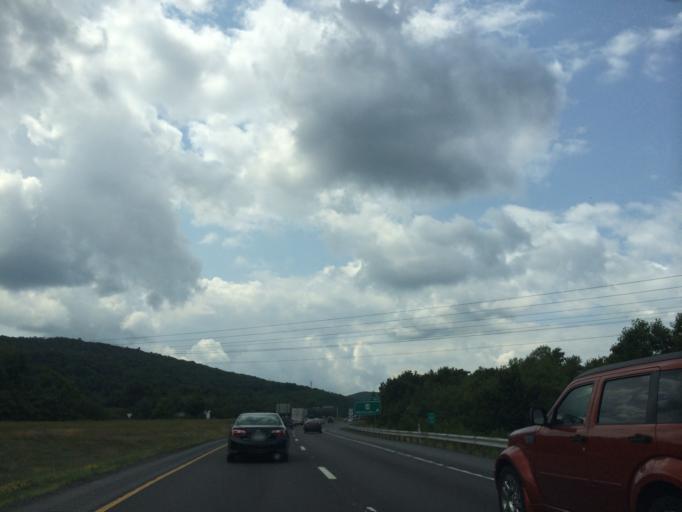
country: US
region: Pennsylvania
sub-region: Luzerne County
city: Ashley
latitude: 41.2062
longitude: -75.9005
